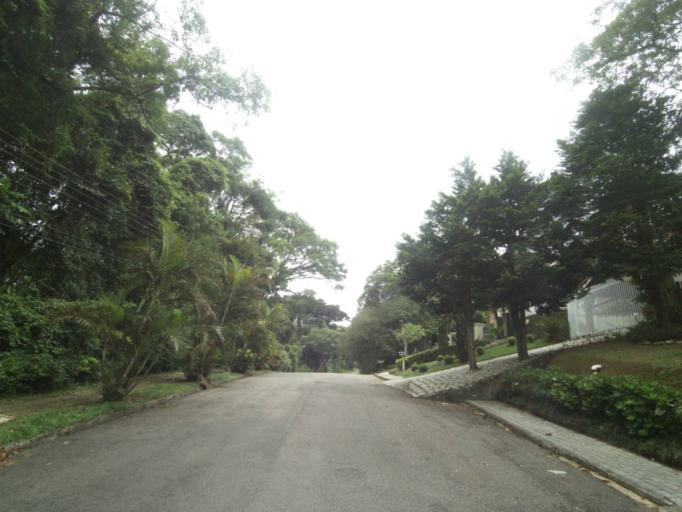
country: BR
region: Parana
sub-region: Curitiba
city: Curitiba
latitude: -25.3908
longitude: -49.2776
